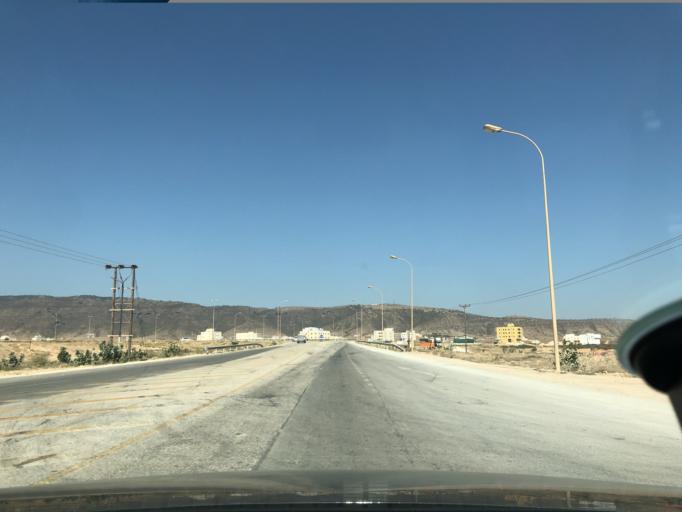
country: OM
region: Zufar
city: Salalah
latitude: 17.0468
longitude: 54.3998
